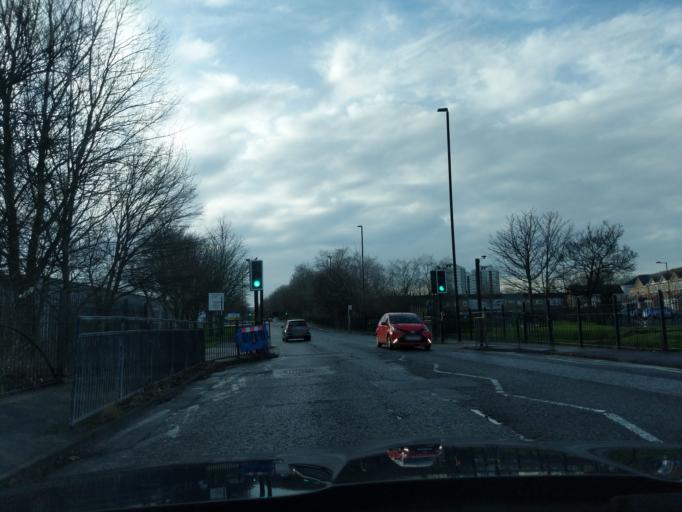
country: GB
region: England
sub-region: Borough of North Tyneside
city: Wallsend
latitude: 54.9879
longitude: -1.5332
